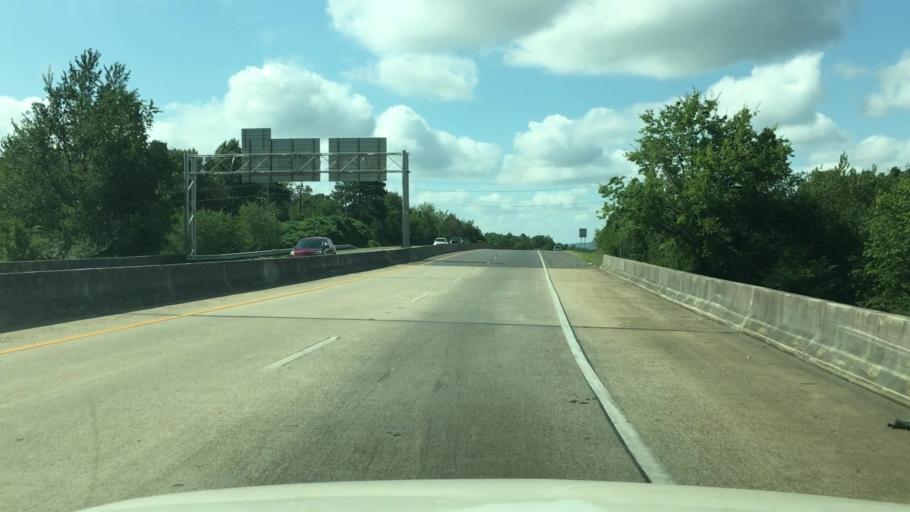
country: US
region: Arkansas
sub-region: Garland County
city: Piney
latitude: 34.4911
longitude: -93.1120
